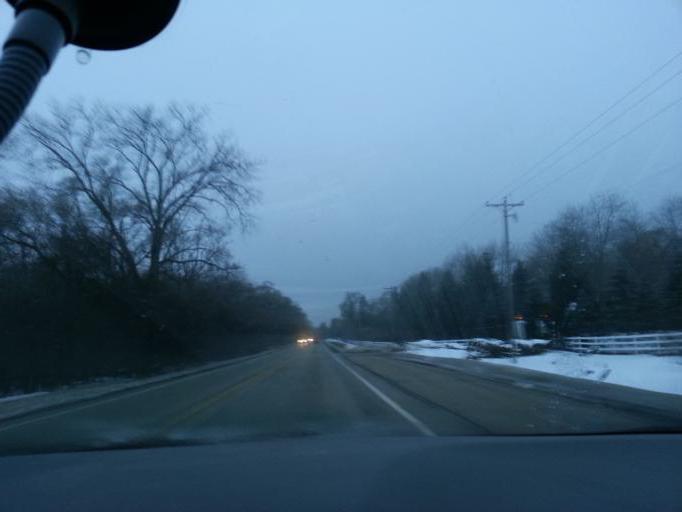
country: US
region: Illinois
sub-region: Cook County
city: Barrington Hills
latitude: 42.1192
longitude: -88.1992
